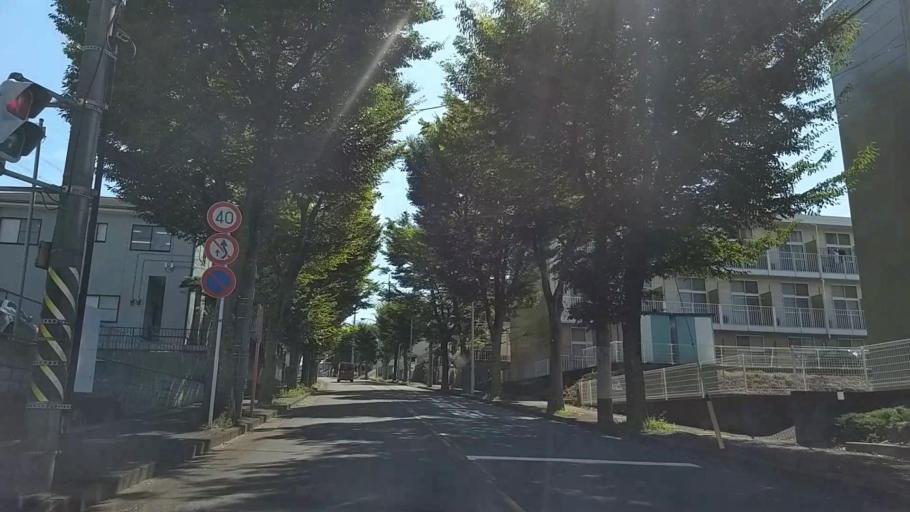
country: JP
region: Tokyo
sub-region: Machida-shi
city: Machida
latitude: 35.5520
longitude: 139.5500
